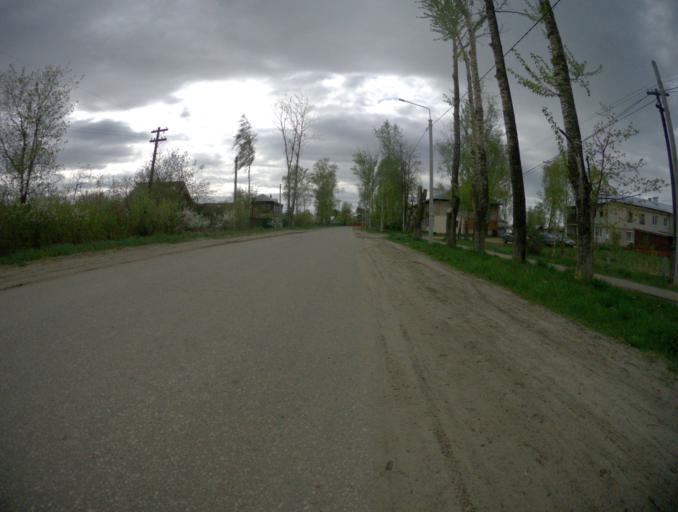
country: RU
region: Vladimir
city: Golovino
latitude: 55.9510
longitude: 40.4378
